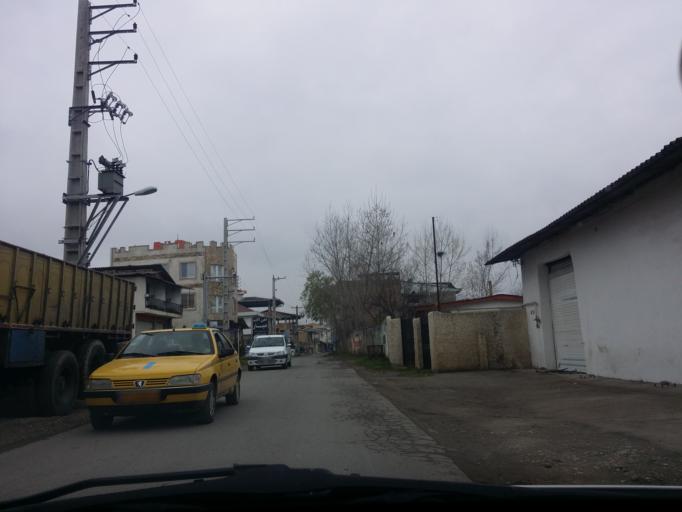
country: IR
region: Mazandaran
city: Chalus
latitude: 36.6657
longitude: 51.3878
